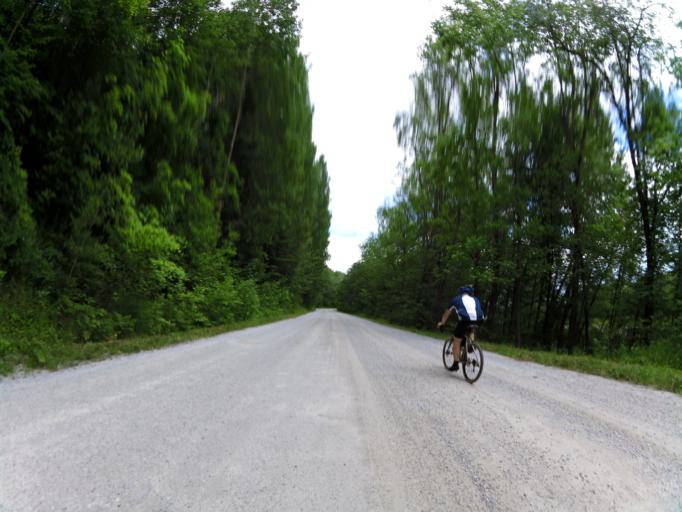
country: CA
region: Ontario
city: Renfrew
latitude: 45.1353
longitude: -76.6563
